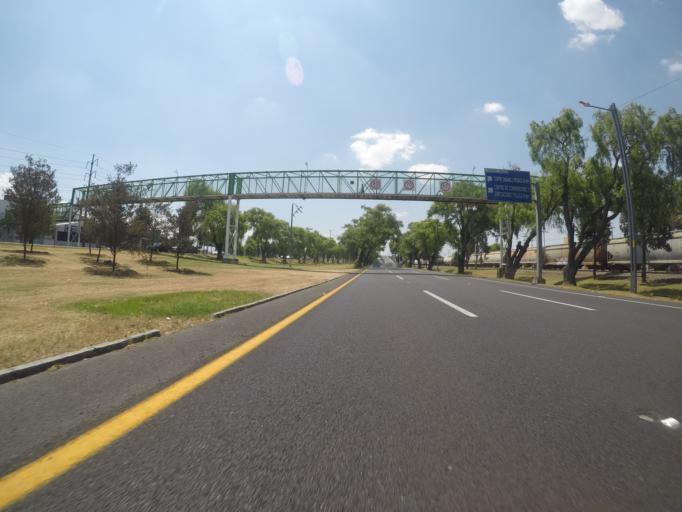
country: MX
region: Mexico
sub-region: San Mateo Atenco
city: Santa Maria la Asuncion
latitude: 19.2862
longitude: -99.5491
